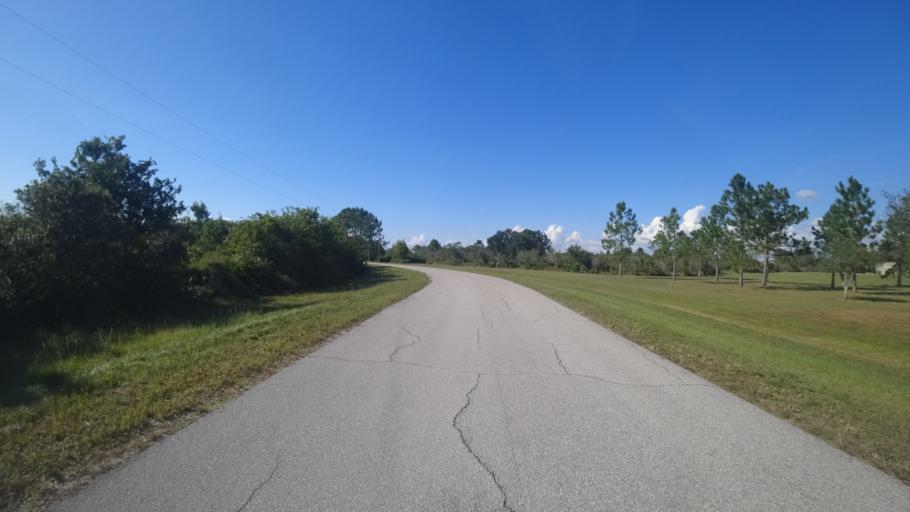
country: US
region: Florida
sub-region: Sarasota County
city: The Meadows
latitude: 27.4164
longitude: -82.2806
